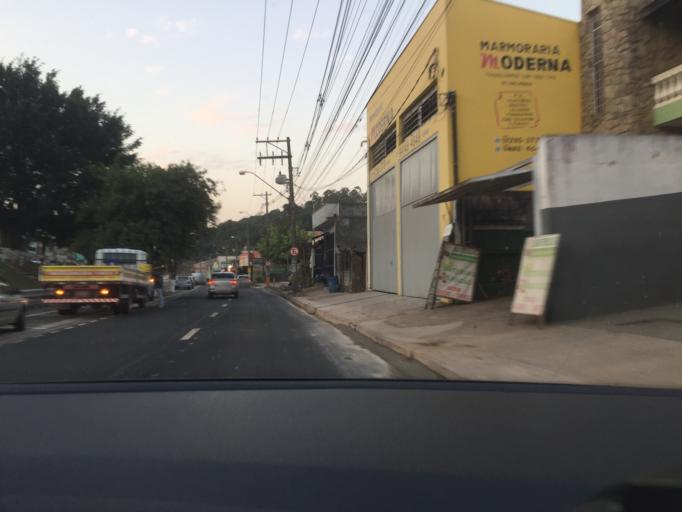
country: BR
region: Sao Paulo
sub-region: Varzea Paulista
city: Varzea Paulista
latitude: -23.2212
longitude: -46.8406
